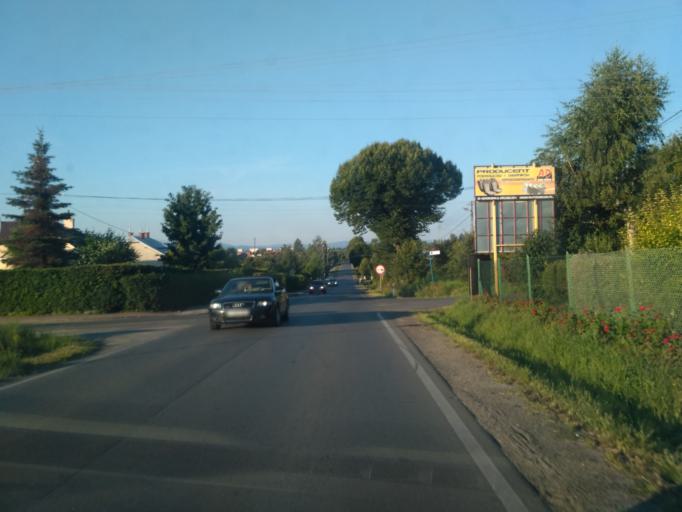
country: PL
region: Subcarpathian Voivodeship
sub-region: Powiat krosnienski
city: Korczyna
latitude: 49.7141
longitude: 21.7949
